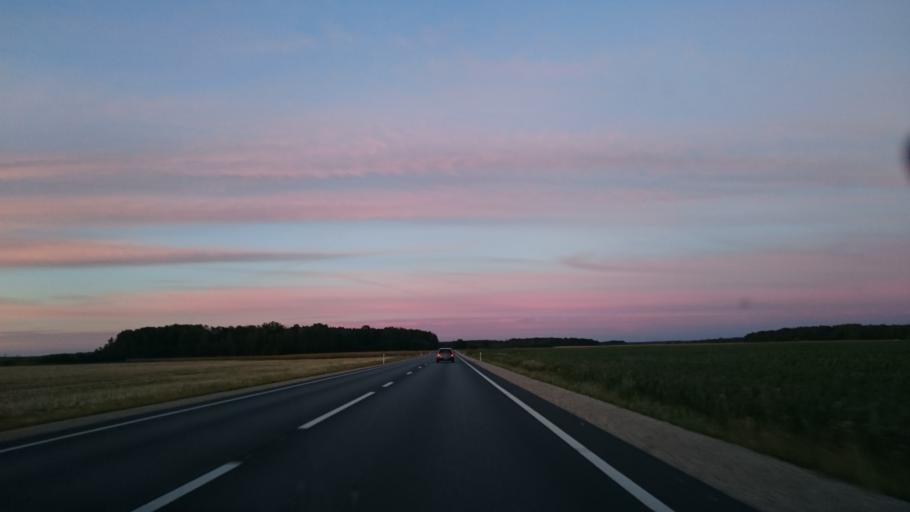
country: LV
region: Dobeles Rajons
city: Dobele
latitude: 56.7643
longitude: 23.3123
